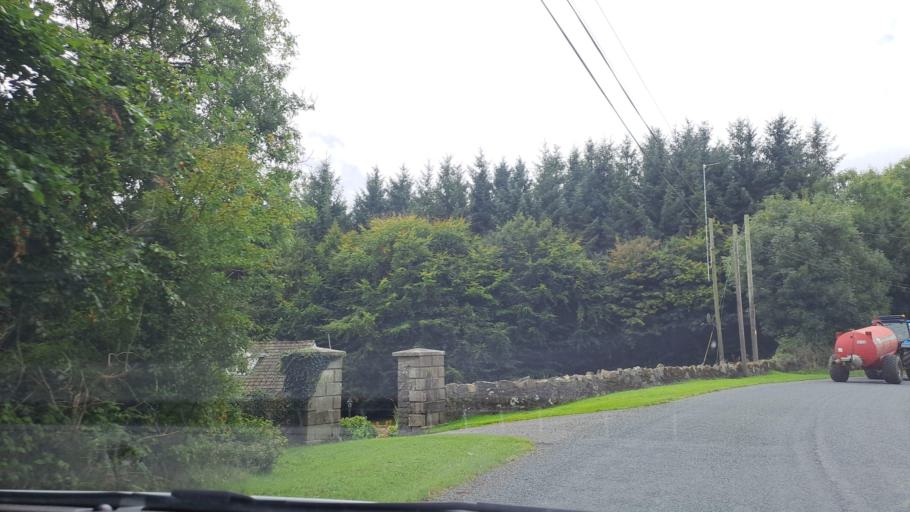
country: IE
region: Ulster
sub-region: An Cabhan
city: Bailieborough
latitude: 53.9942
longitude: -6.9150
